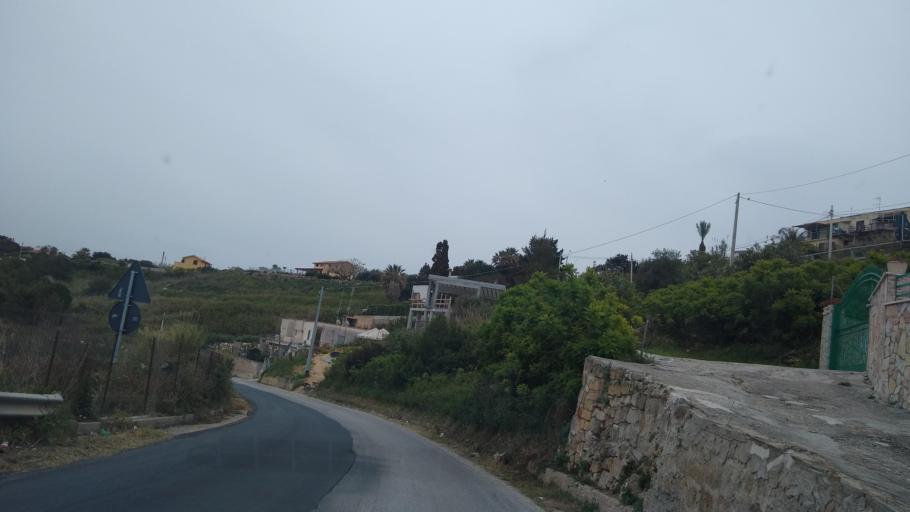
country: IT
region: Sicily
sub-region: Trapani
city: Castellammare del Golfo
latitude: 38.0220
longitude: 12.8970
